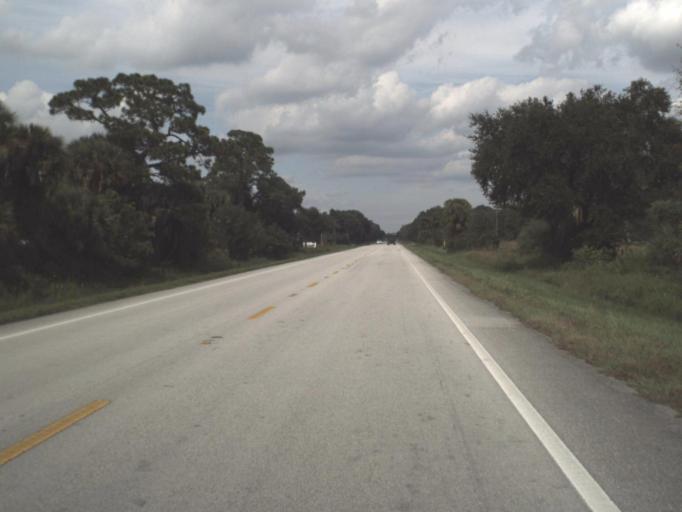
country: US
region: Florida
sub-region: Okeechobee County
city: Cypress Quarters
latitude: 27.3534
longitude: -80.8210
